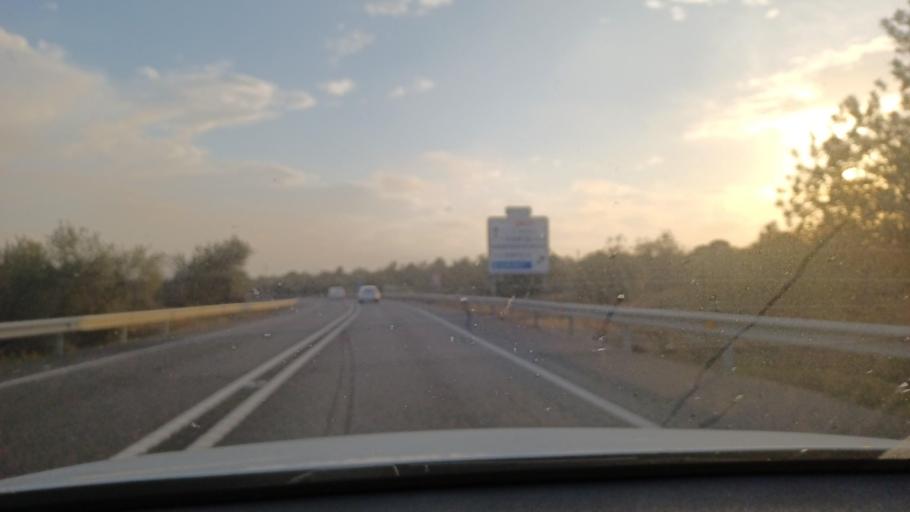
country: ES
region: Catalonia
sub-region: Provincia de Tarragona
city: L'Ampolla
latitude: 40.8178
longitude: 0.7049
